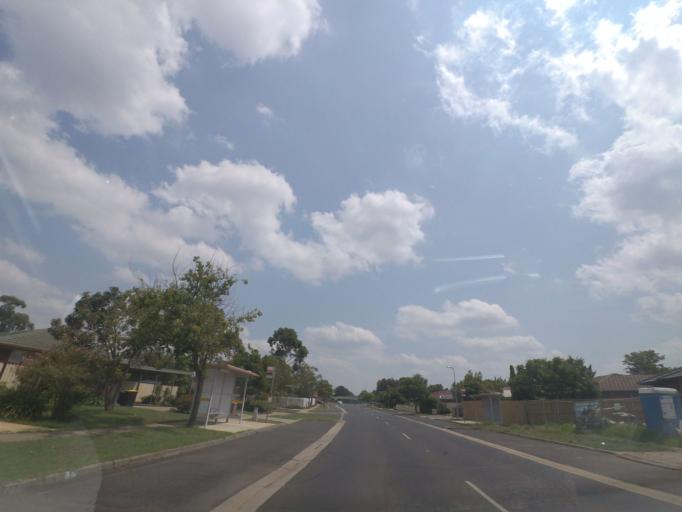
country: AU
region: Victoria
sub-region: Melton
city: Melton West
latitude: -37.6785
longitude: 144.5617
